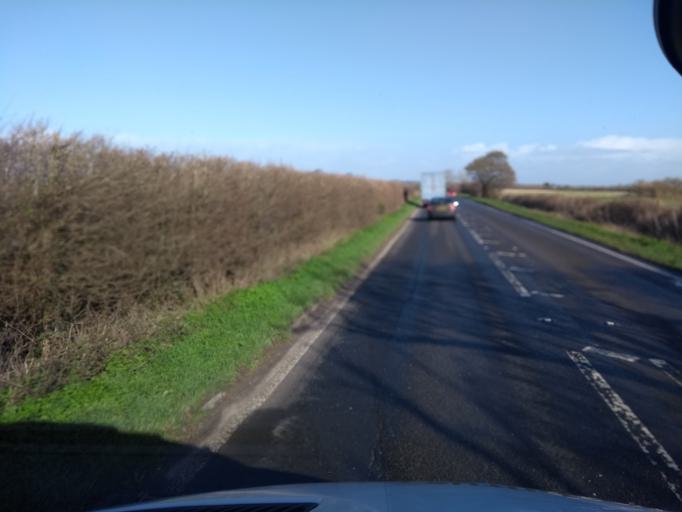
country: GB
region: England
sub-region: Somerset
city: Ilchester
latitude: 50.9877
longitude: -2.6771
